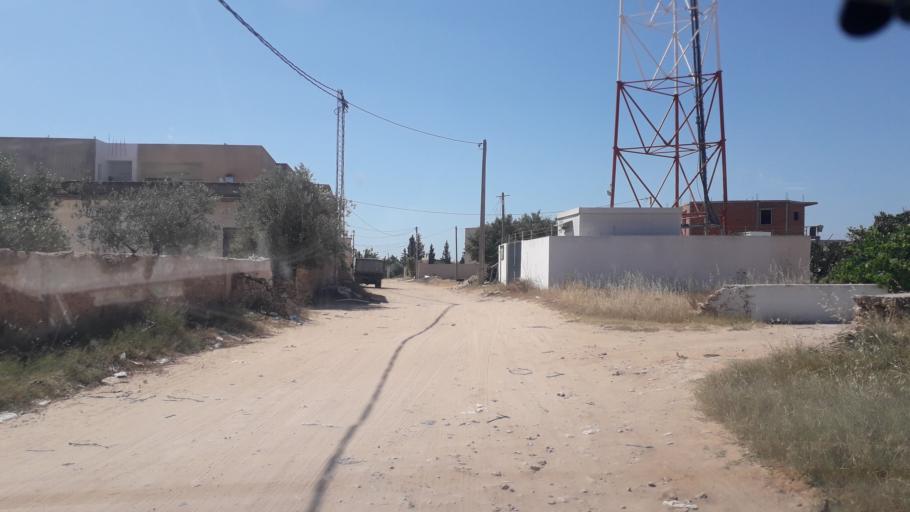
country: TN
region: Safaqis
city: Al Qarmadah
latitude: 34.8277
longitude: 10.7668
